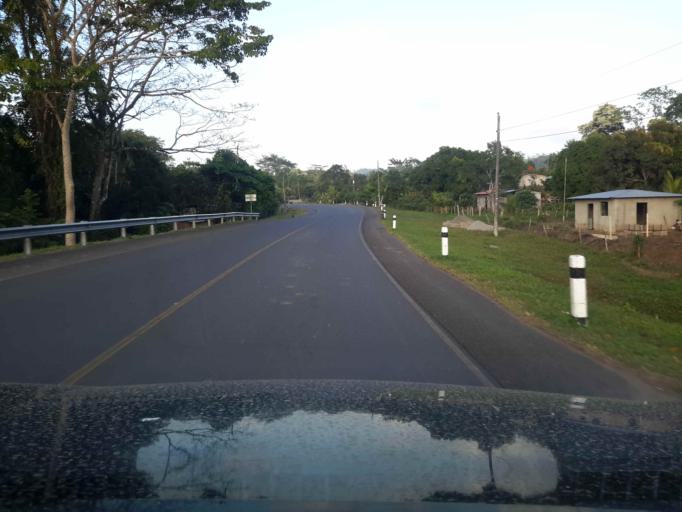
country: NI
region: Rio San Juan
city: San Carlos
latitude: 11.2299
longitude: -84.6910
